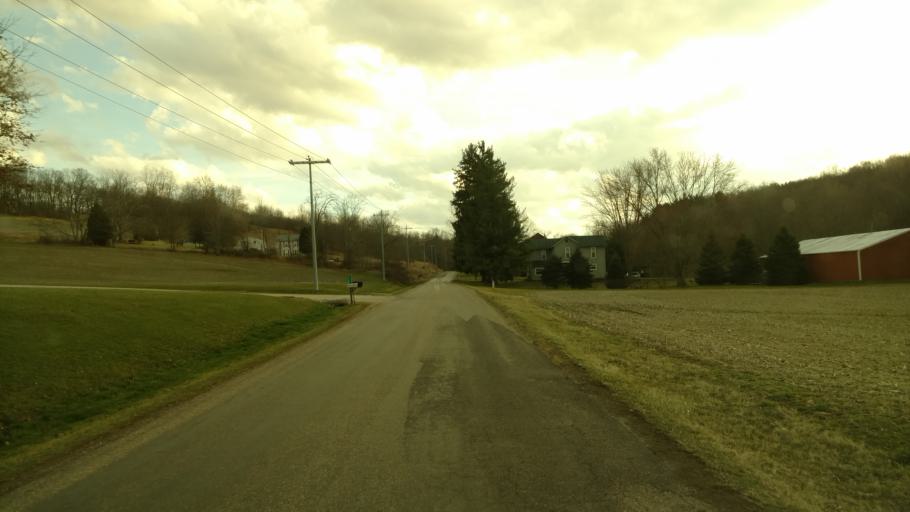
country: US
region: Ohio
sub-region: Sandusky County
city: Bellville
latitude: 40.5642
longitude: -82.4505
